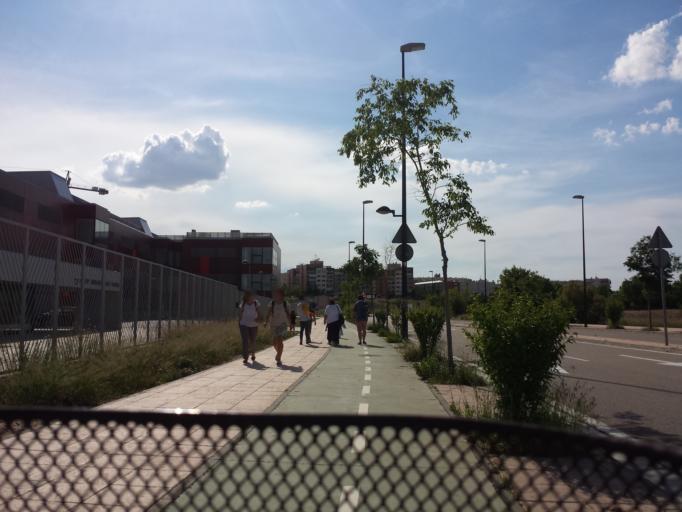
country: ES
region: Aragon
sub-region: Provincia de Zaragoza
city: Montecanal
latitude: 41.6358
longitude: -0.9395
